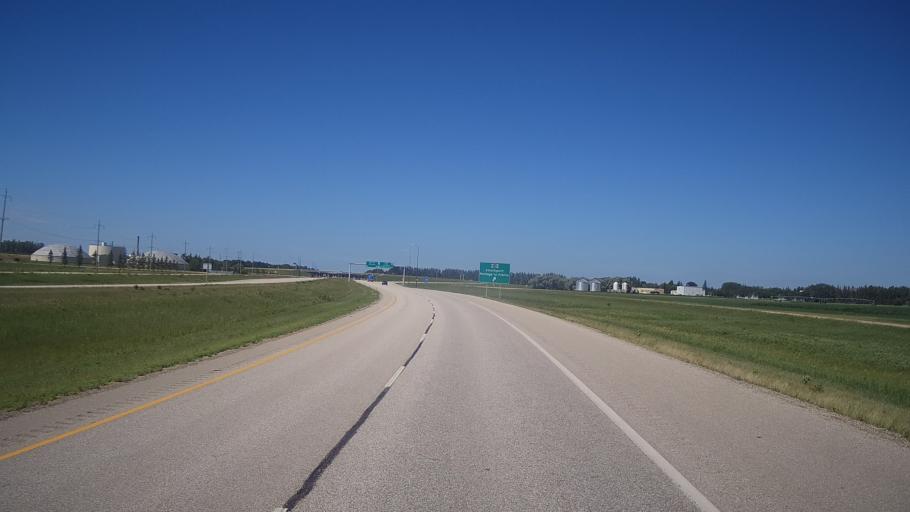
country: CA
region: Manitoba
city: Portage la Prairie
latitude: 49.9584
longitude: -98.2632
